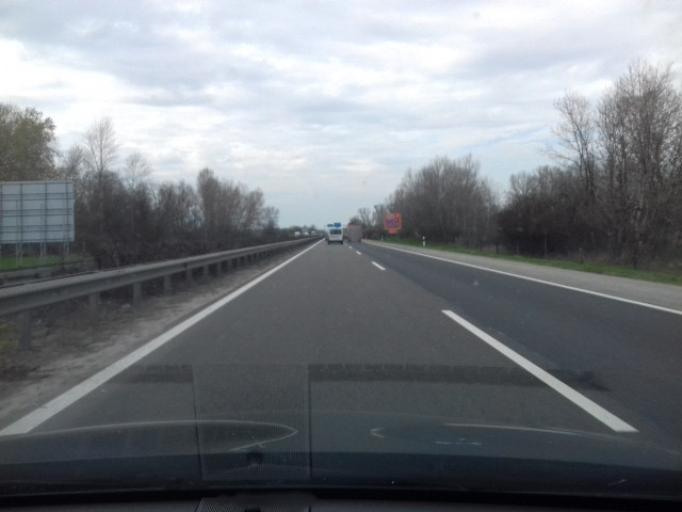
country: HU
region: Pest
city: Gyal
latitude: 47.3831
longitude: 19.1776
